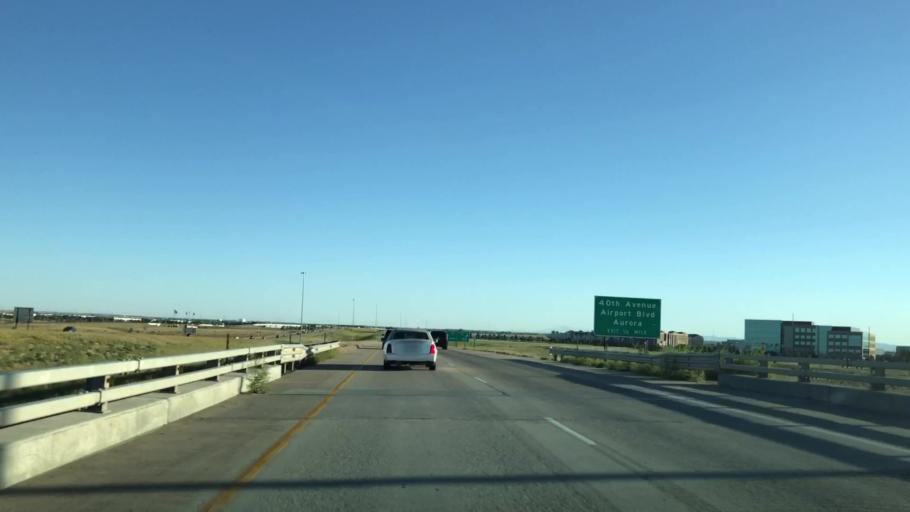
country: US
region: Colorado
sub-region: Adams County
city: Aurora
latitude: 39.7836
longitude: -104.7915
